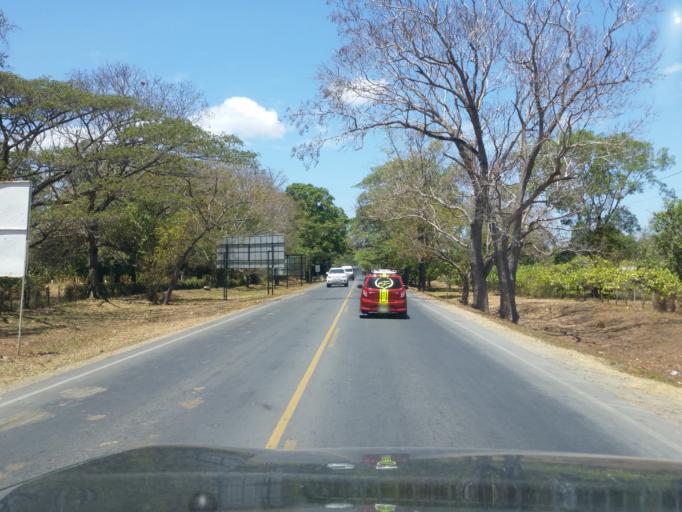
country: NI
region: Rivas
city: Buenos Aires
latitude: 11.4624
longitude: -85.8480
